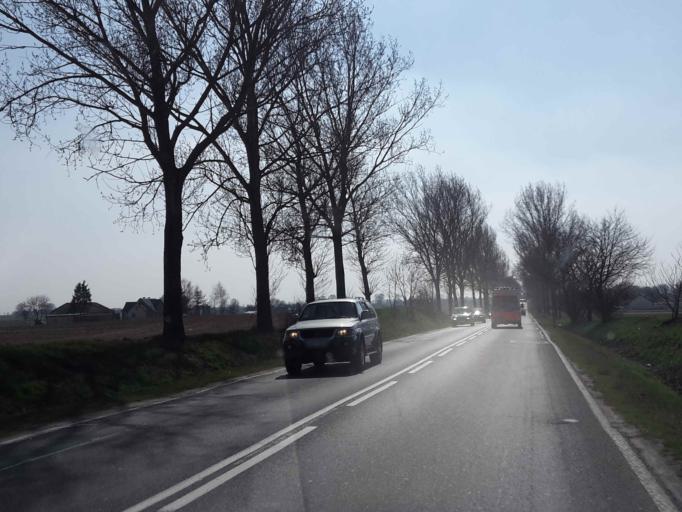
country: PL
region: Kujawsko-Pomorskie
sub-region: Powiat golubsko-dobrzynski
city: Kowalewo Pomorskie
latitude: 53.1411
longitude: 18.8624
